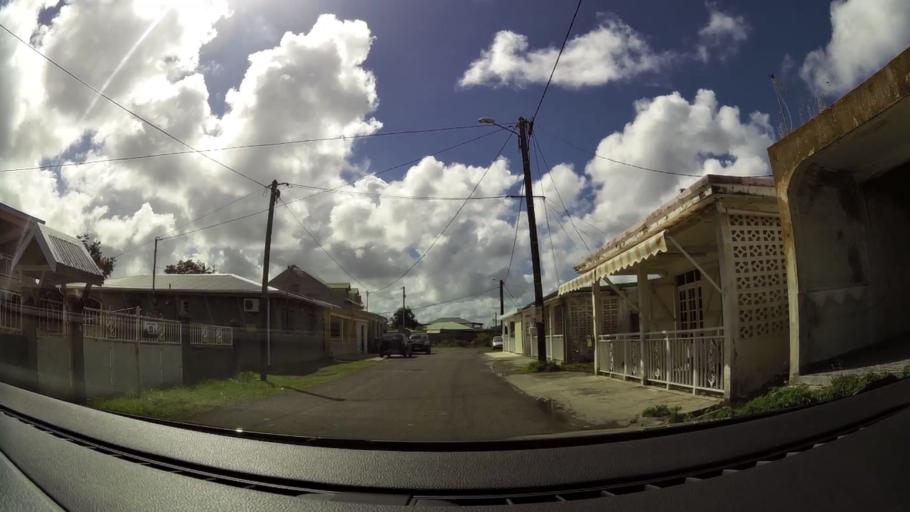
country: GP
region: Guadeloupe
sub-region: Guadeloupe
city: Anse-Bertrand
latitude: 16.4701
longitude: -61.5072
